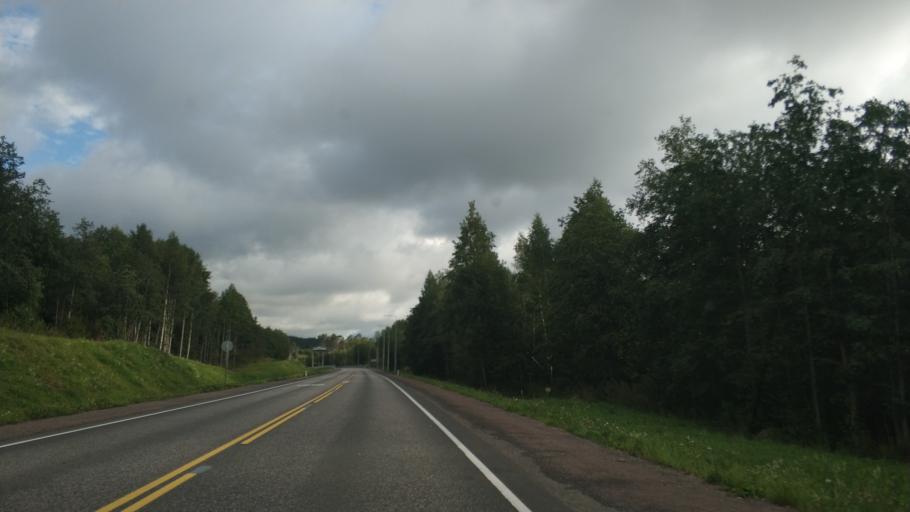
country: RU
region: Republic of Karelia
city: Khelyulya
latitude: 61.8143
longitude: 30.6291
